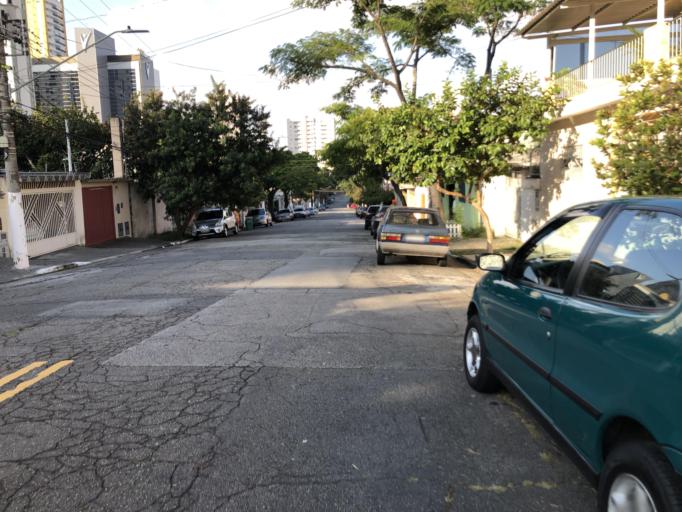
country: BR
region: Sao Paulo
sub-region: Diadema
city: Diadema
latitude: -23.6196
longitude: -46.6333
